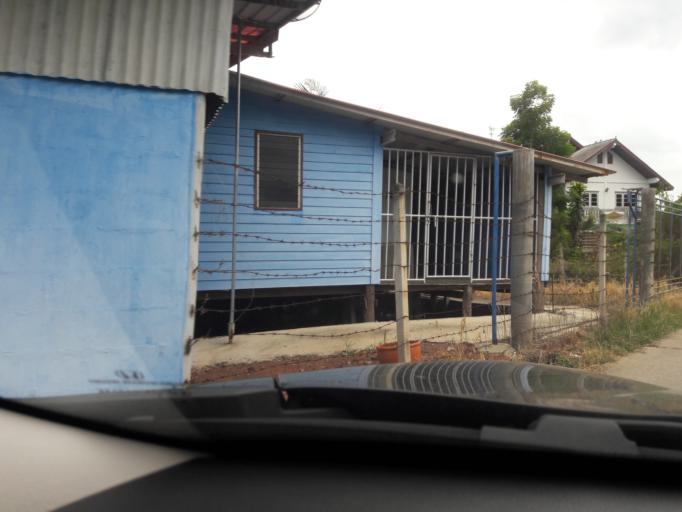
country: TH
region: Ratchaburi
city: Damnoen Saduak
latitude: 13.5898
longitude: 99.9391
